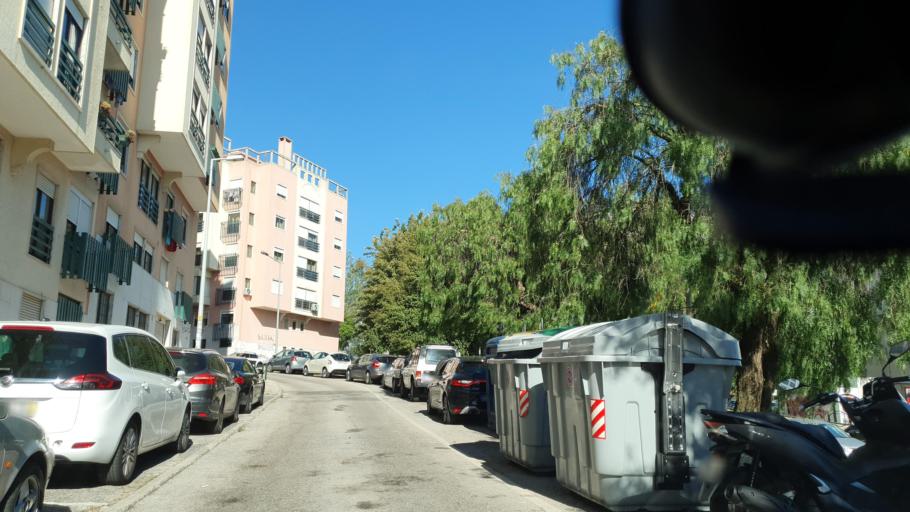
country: PT
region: Lisbon
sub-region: Oeiras
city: Barcarena
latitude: 38.7519
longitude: -9.2788
